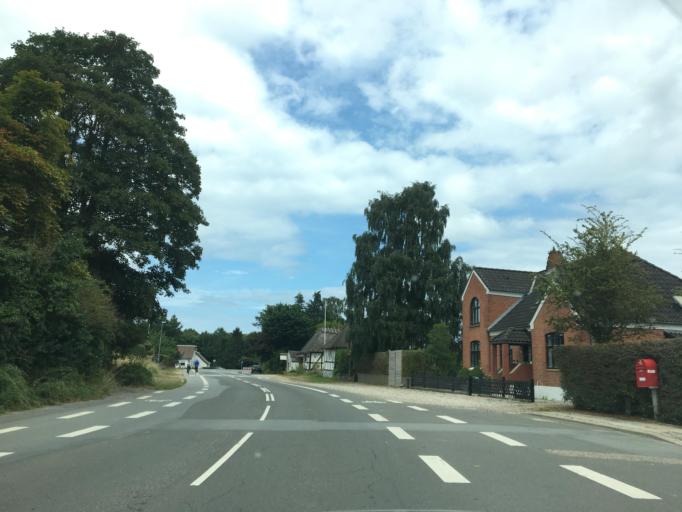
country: DK
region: South Denmark
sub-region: Nyborg Kommune
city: Nyborg
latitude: 55.3110
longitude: 10.7369
